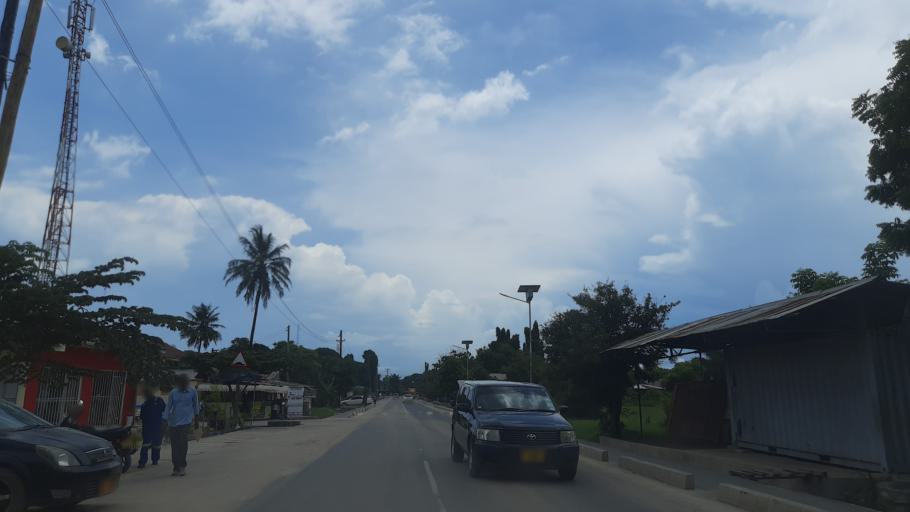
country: TZ
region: Dar es Salaam
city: Magomeni
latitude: -6.7744
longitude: 39.2296
